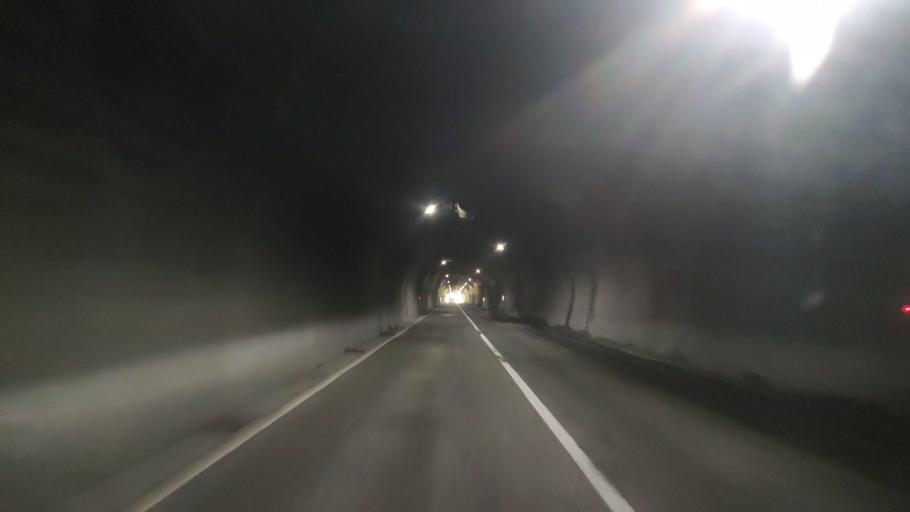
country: JP
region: Fukui
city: Tsuruga
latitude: 35.7677
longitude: 136.1059
